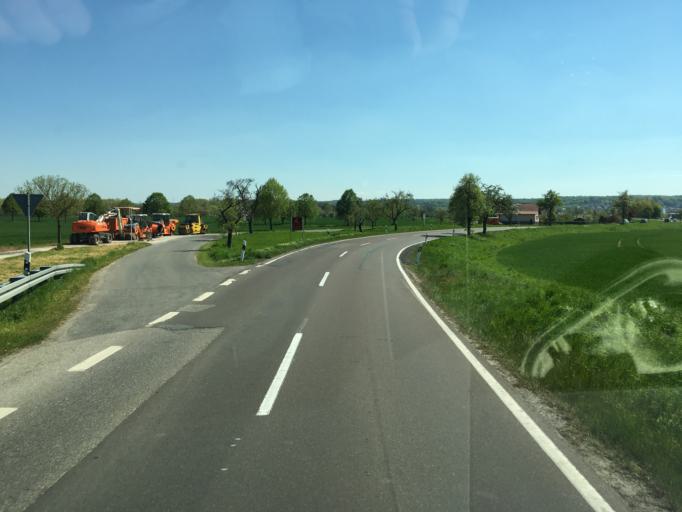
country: DE
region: Saxony-Anhalt
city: Naumburg
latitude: 51.1756
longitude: 11.7821
